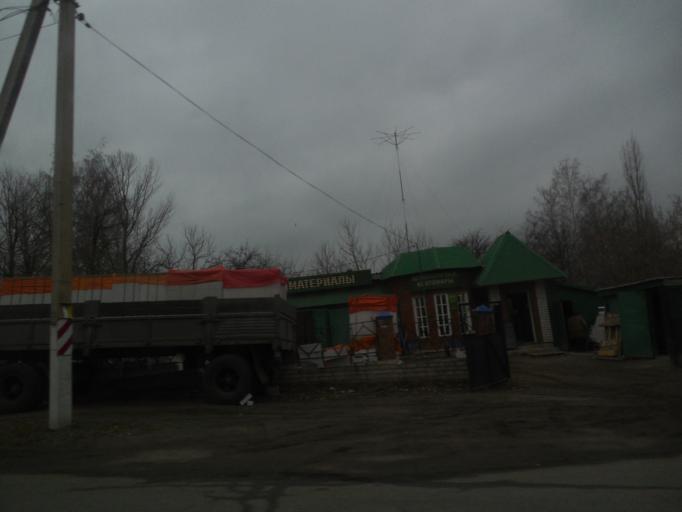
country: RU
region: Lipetsk
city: Zadonsk
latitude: 52.3897
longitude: 38.9315
